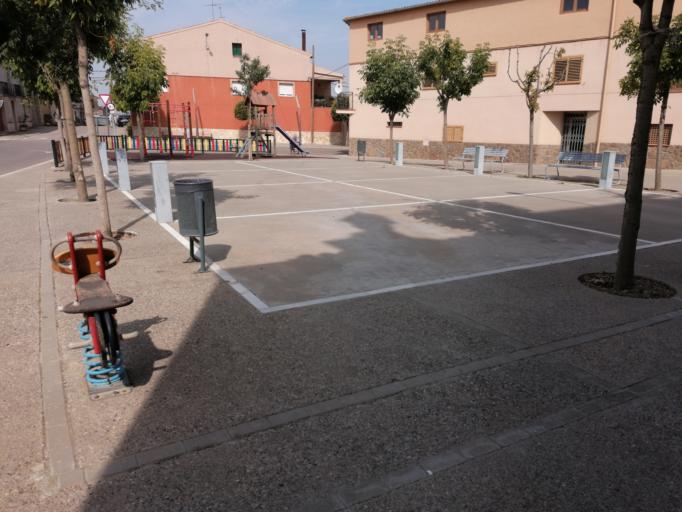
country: ES
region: Catalonia
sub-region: Provincia de Lleida
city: Bellvis
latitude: 41.6939
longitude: 0.8321
